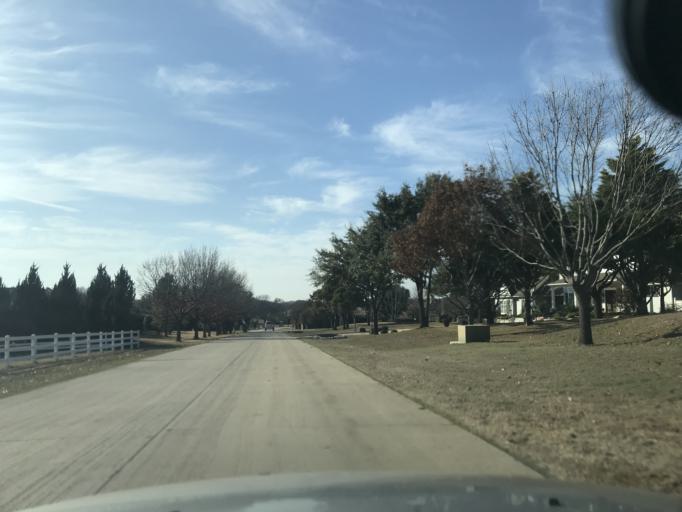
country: US
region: Texas
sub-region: Collin County
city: Frisco
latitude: 33.0947
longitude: -96.8278
